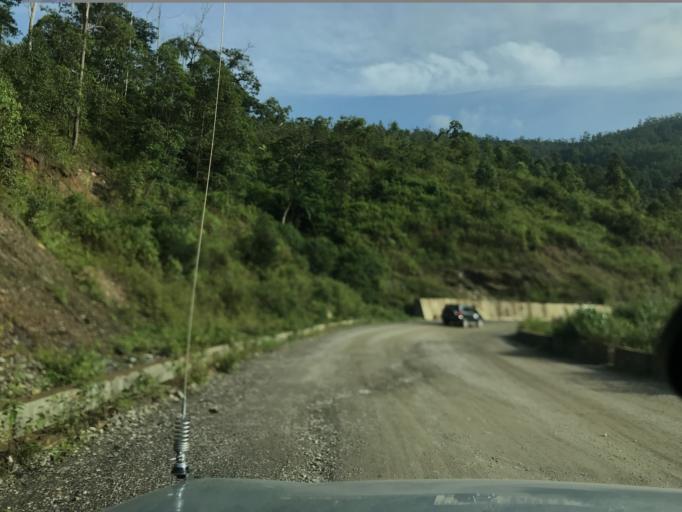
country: TL
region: Aileu
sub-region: Aileu Villa
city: Aileu
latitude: -8.6629
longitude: 125.5474
